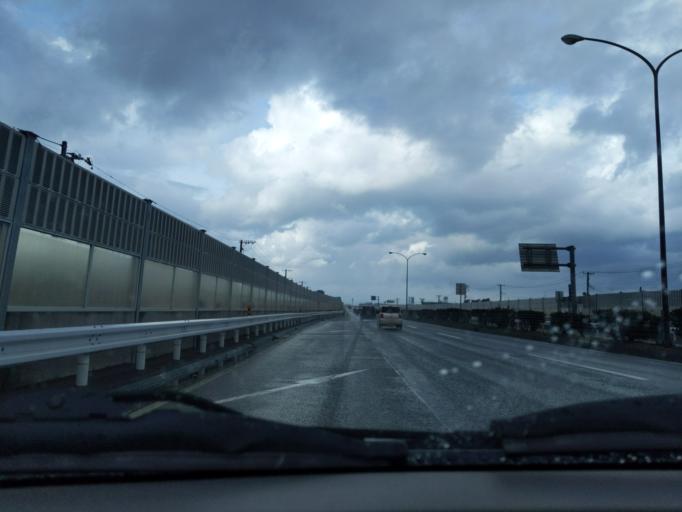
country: JP
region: Niigata
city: Kameda-honcho
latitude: 37.8856
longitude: 139.0784
